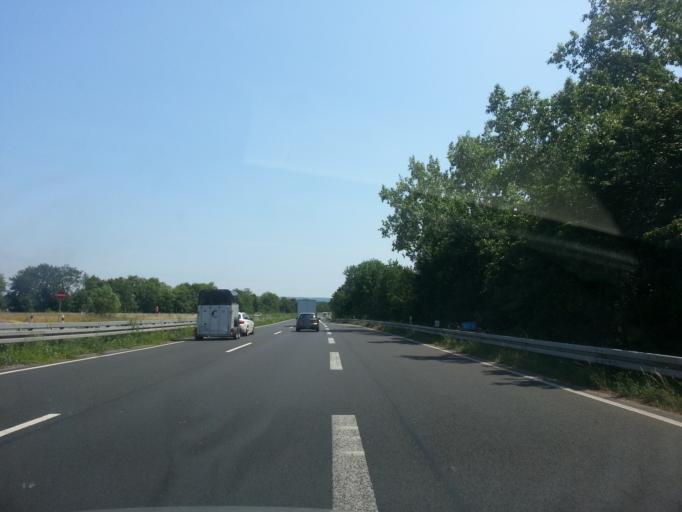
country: DE
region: Hesse
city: Dieburg
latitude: 49.9125
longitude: 8.8519
